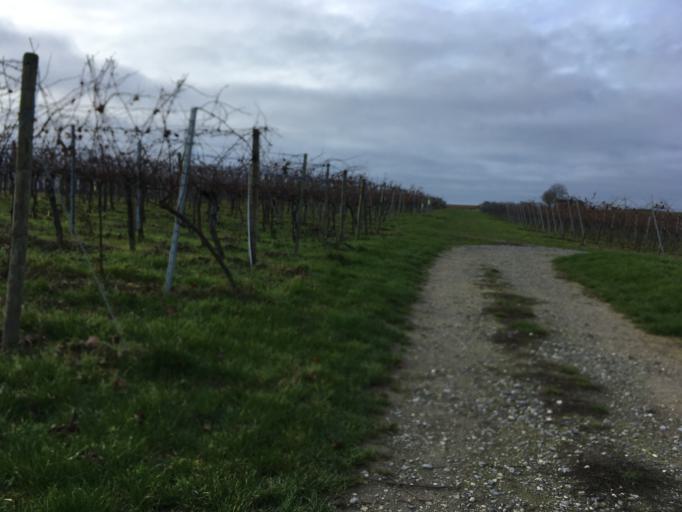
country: DE
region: Baden-Wuerttemberg
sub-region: Regierungsbezirk Stuttgart
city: Lauffen am Neckar
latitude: 49.0820
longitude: 9.1427
